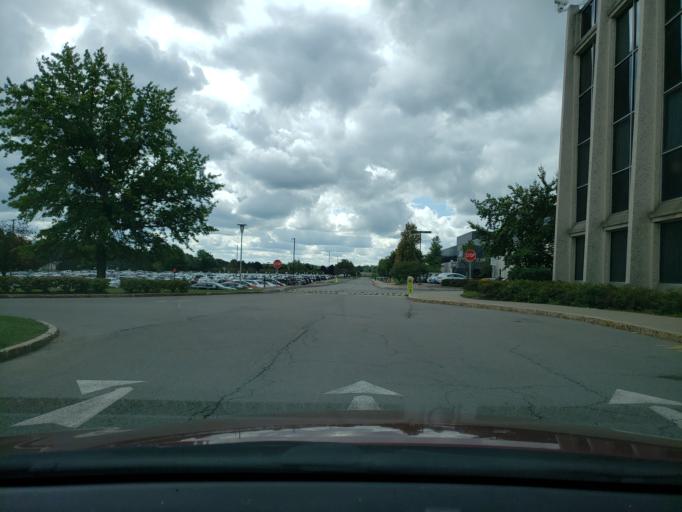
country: US
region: New York
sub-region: Monroe County
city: North Gates
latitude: 43.1520
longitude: -77.7345
